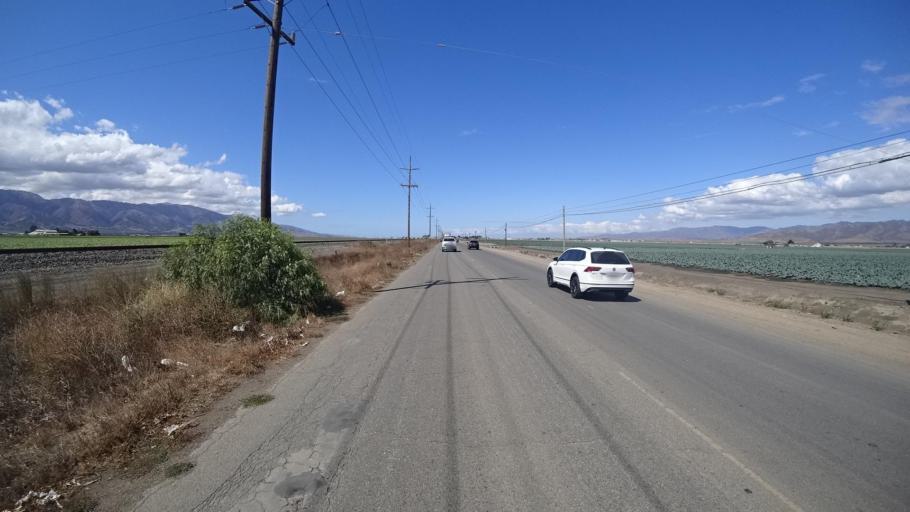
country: US
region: California
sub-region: Monterey County
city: Gonzales
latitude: 36.5196
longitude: -121.4523
